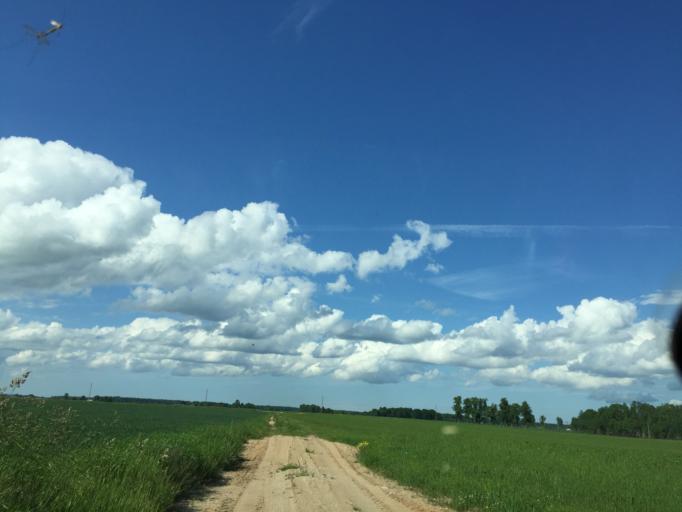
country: LV
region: Dobeles Rajons
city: Dobele
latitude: 56.6834
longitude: 23.4001
